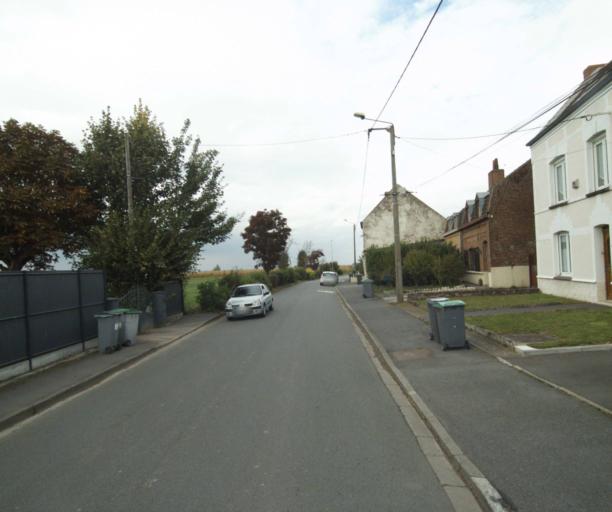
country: FR
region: Nord-Pas-de-Calais
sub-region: Departement du Nord
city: Salome
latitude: 50.5343
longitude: 2.8356
